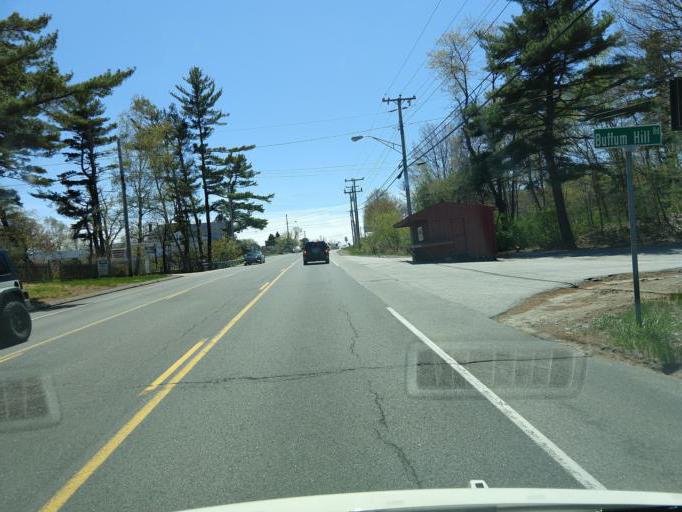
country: US
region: Maine
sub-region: York County
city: Wells Beach Station
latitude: 43.2971
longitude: -70.5877
